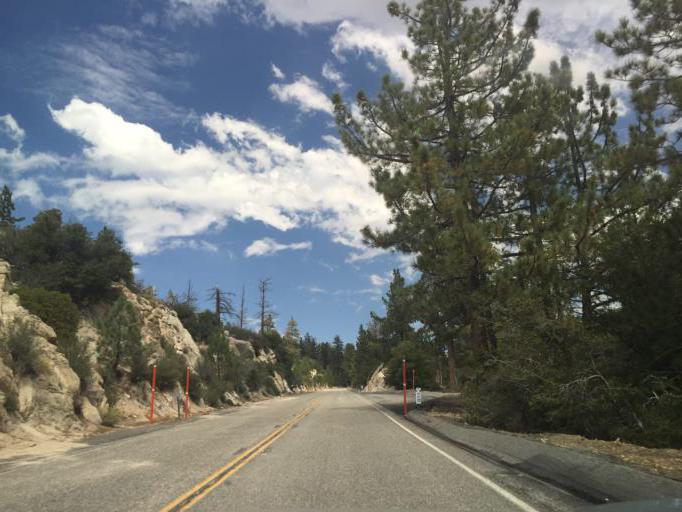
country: US
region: California
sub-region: Los Angeles County
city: Littlerock
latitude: 34.3452
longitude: -117.9702
